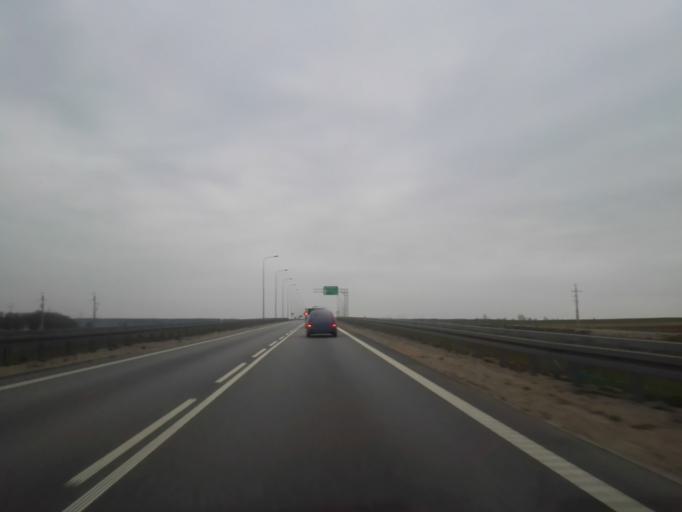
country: PL
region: Podlasie
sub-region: Powiat kolnenski
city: Stawiski
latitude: 53.3954
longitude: 22.1530
